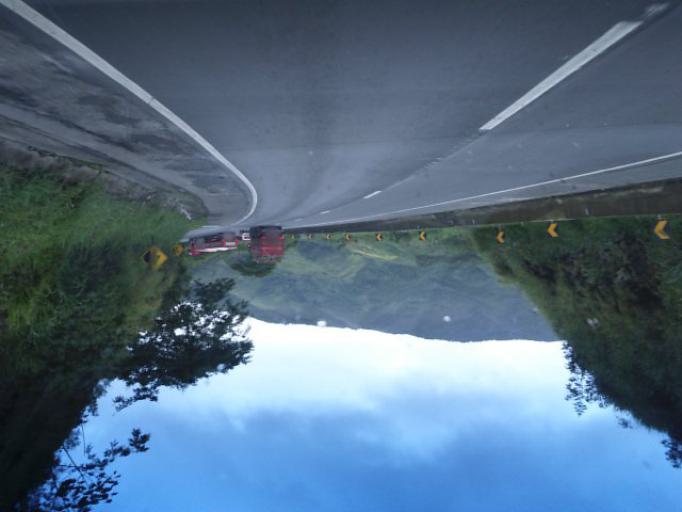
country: BR
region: Sao Paulo
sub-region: Cajati
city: Cajati
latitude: -24.8484
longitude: -48.2142
